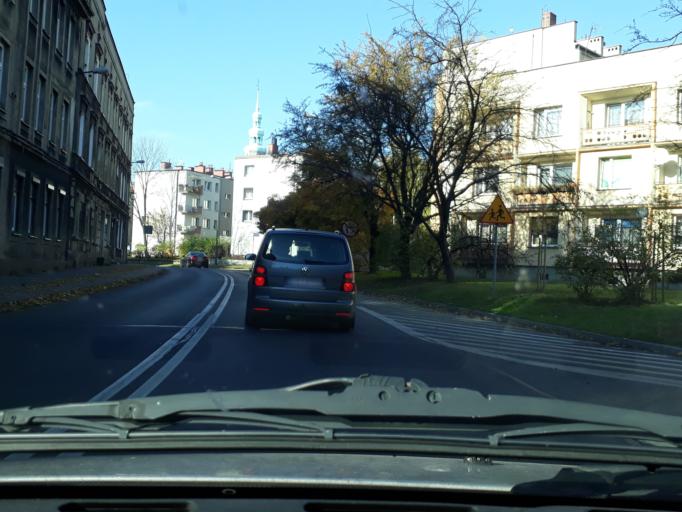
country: PL
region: Silesian Voivodeship
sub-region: Powiat tarnogorski
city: Tarnowskie Gory
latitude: 50.4416
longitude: 18.8554
